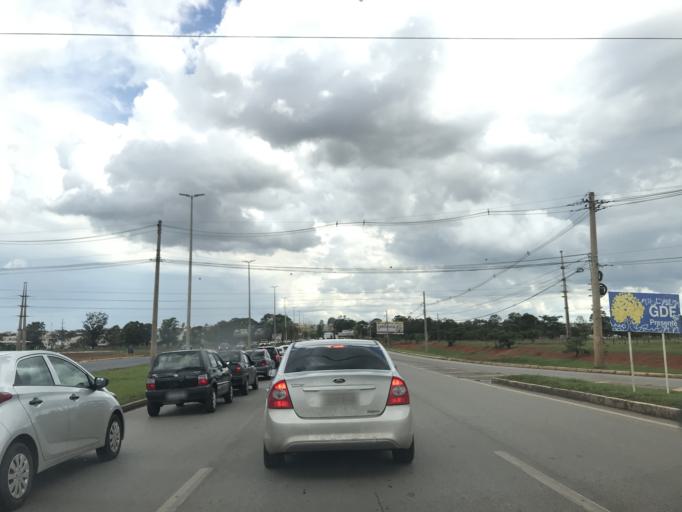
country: BR
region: Federal District
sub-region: Brasilia
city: Brasilia
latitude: -15.8843
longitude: -48.0592
